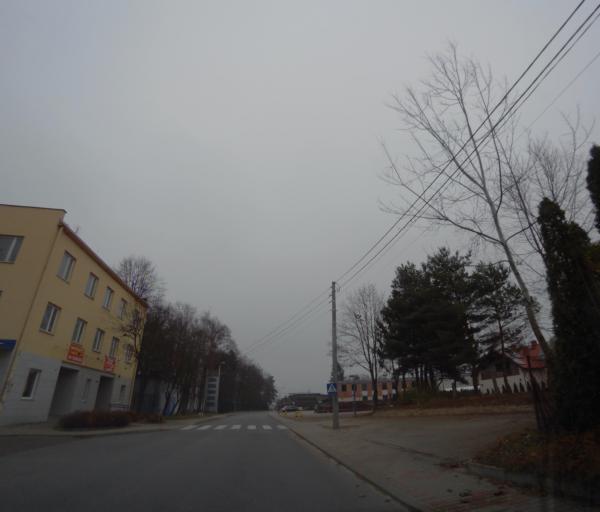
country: PL
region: Subcarpathian Voivodeship
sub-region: Powiat lezajski
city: Lezajsk
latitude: 50.2695
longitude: 22.4205
